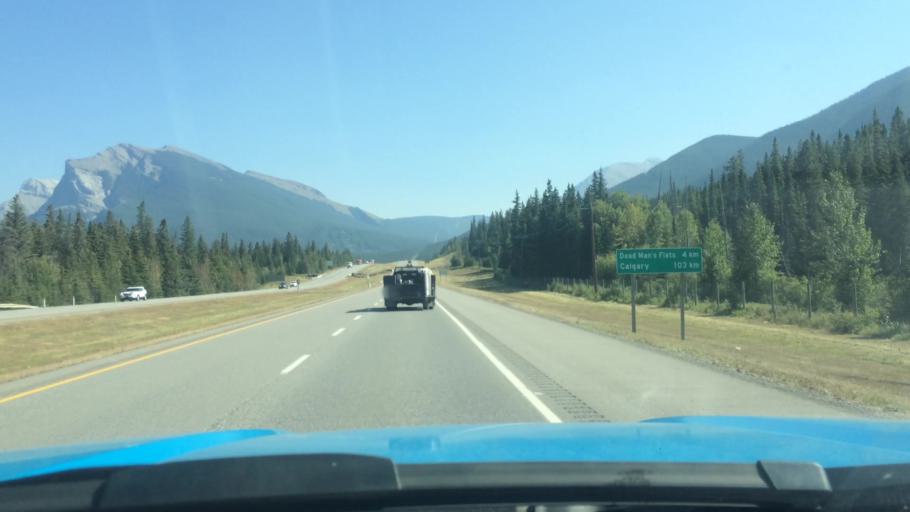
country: CA
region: Alberta
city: Canmore
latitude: 51.0498
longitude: -115.3012
